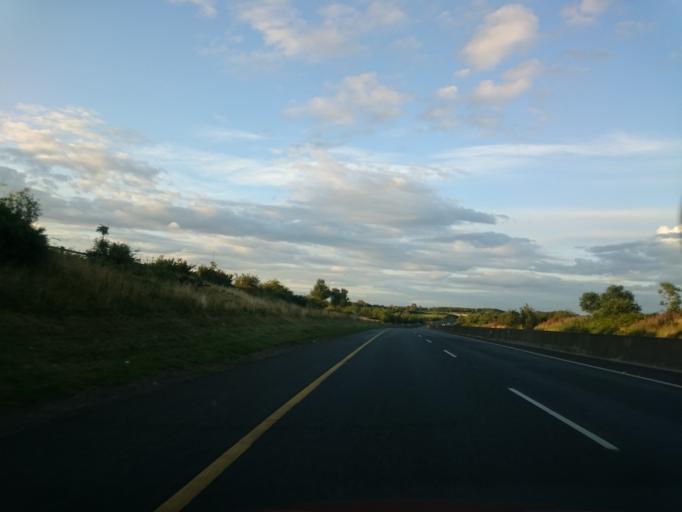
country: IE
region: Leinster
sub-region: Loch Garman
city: Castletown
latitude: 52.7358
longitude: -6.2342
